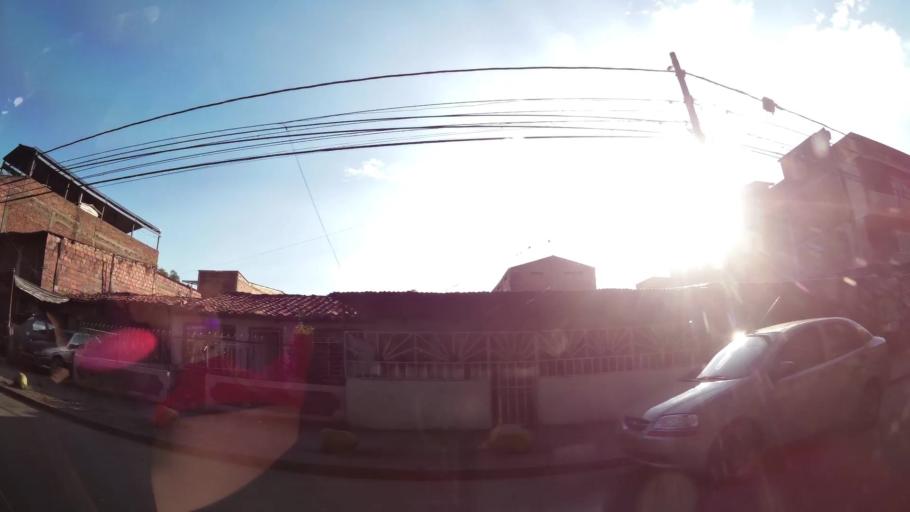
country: CO
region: Valle del Cauca
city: Cali
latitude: 3.4100
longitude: -76.5059
